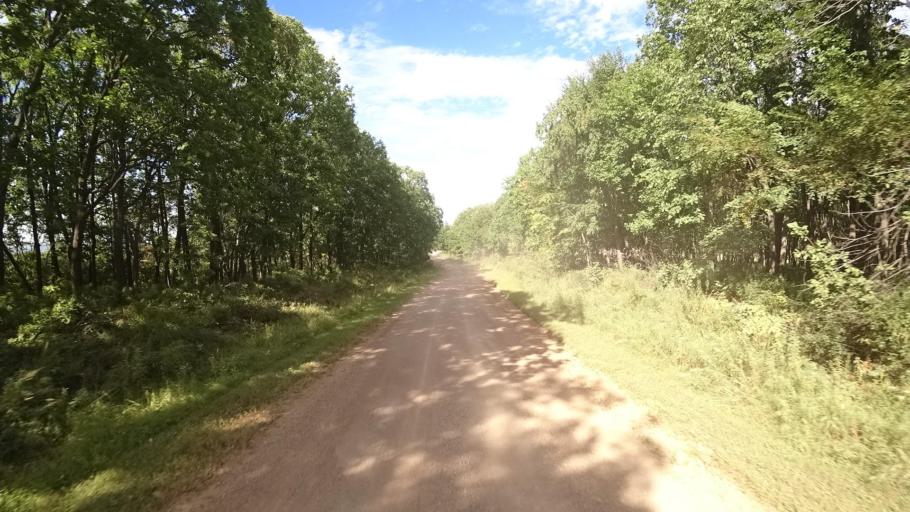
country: RU
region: Primorskiy
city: Yakovlevka
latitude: 44.4141
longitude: 133.5701
